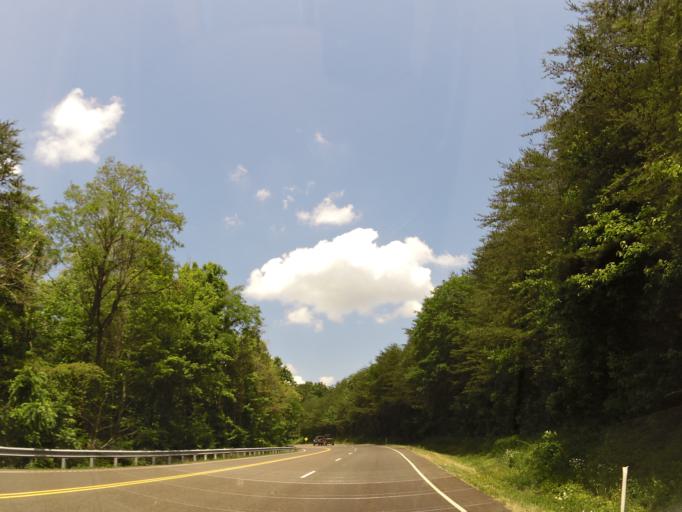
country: US
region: Tennessee
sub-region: Rhea County
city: Dayton
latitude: 35.5082
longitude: -85.0401
